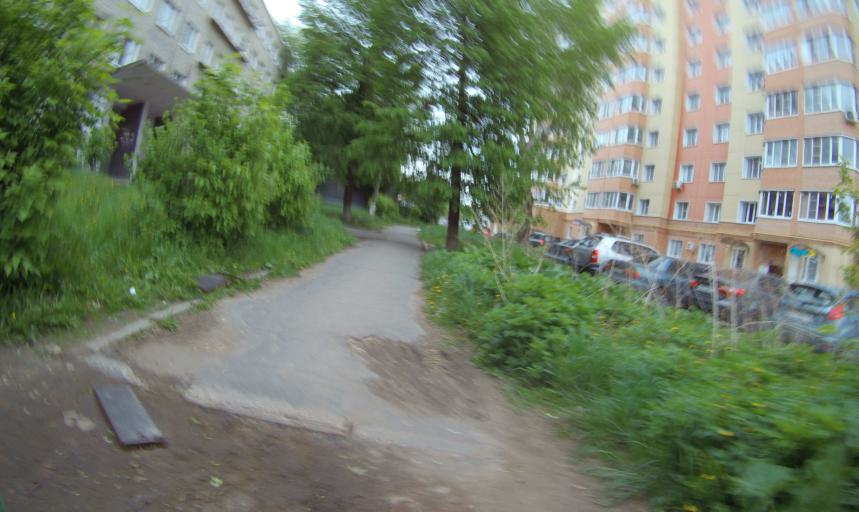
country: RU
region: Moskovskaya
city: Kolomna
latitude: 55.0801
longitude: 38.8050
